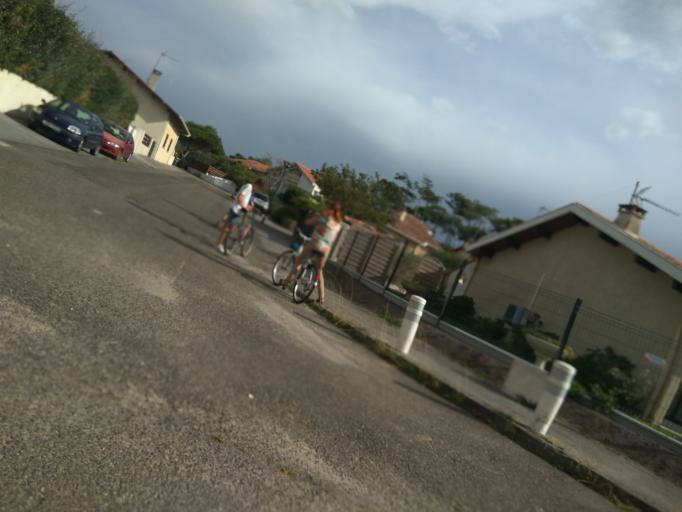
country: FR
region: Aquitaine
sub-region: Departement des Landes
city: Capbreton
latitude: 43.6337
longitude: -1.4457
